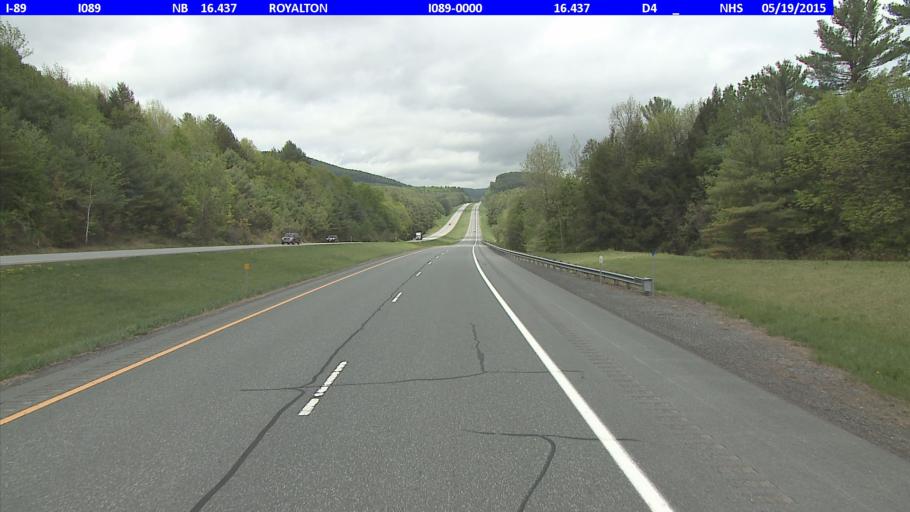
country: US
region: Vermont
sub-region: Windsor County
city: Woodstock
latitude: 43.7949
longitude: -72.5056
